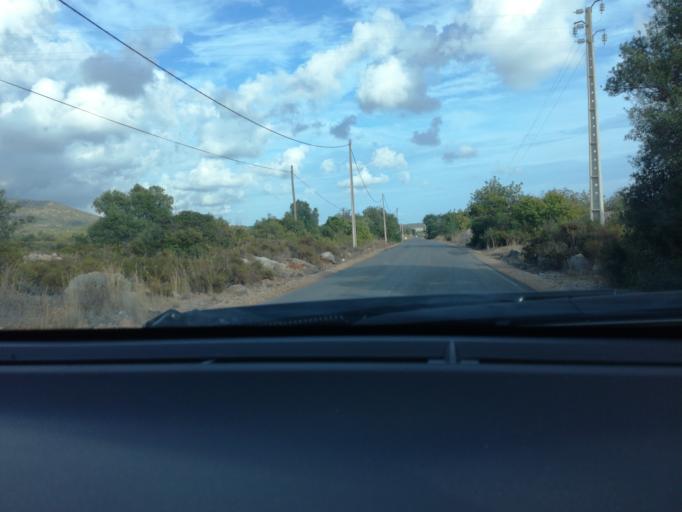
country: PT
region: Faro
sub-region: Olhao
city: Olhao
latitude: 37.0820
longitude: -7.8519
